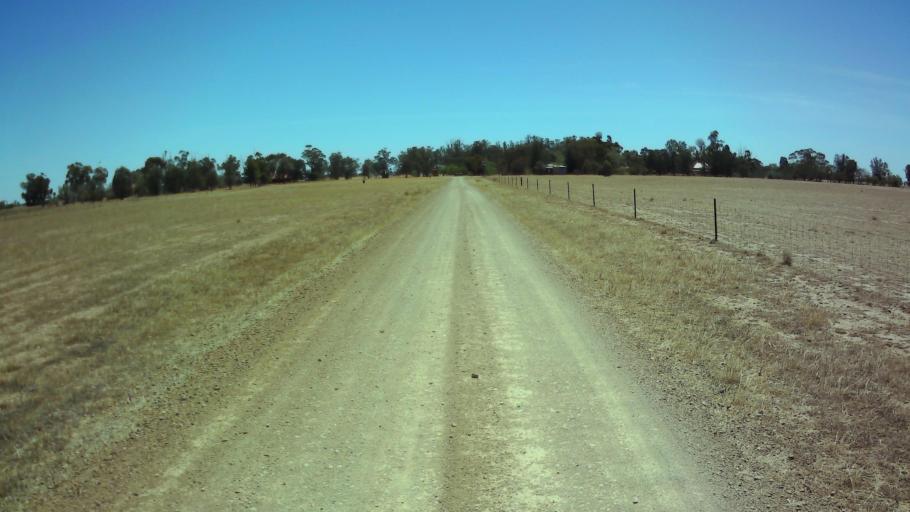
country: AU
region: New South Wales
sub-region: Weddin
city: Grenfell
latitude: -33.9969
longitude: 147.7354
